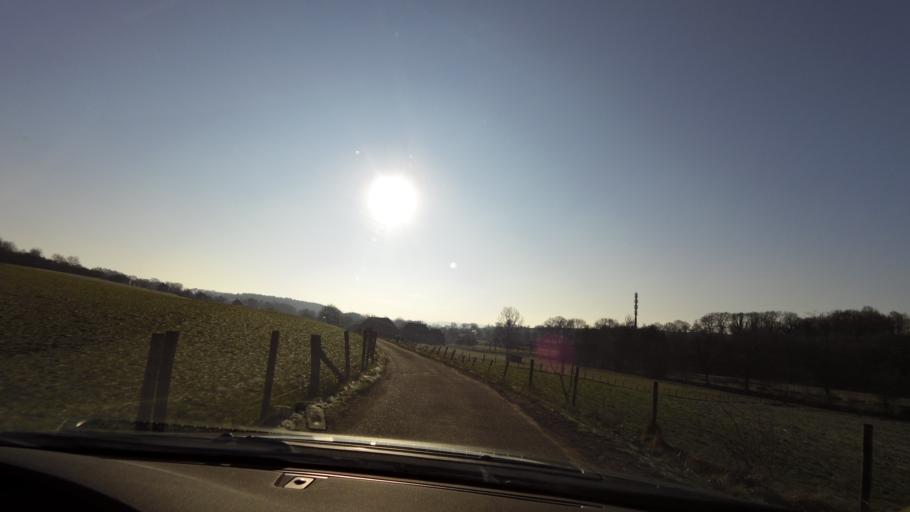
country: NL
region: Limburg
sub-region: Gemeente Simpelveld
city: Simpelveld
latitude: 50.8114
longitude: 5.9504
